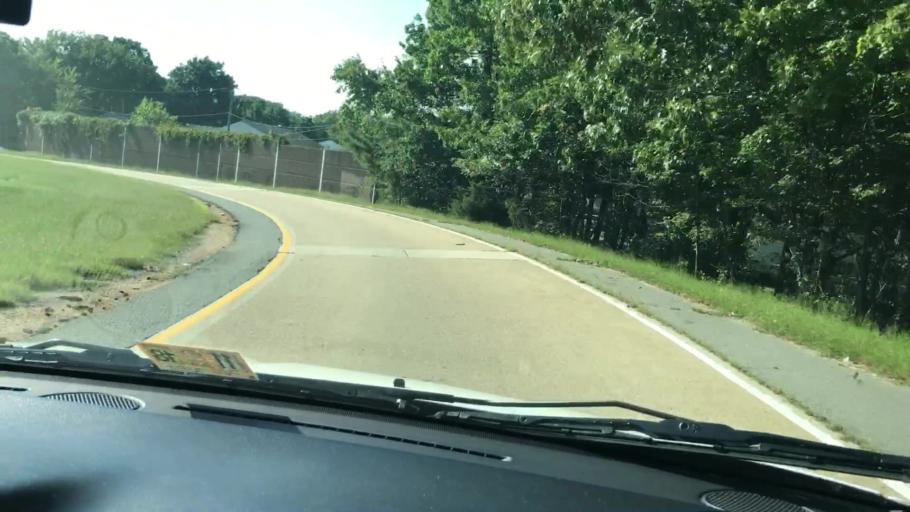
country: US
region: Virginia
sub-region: City of Norfolk
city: Norfolk
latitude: 36.8929
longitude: -76.2301
